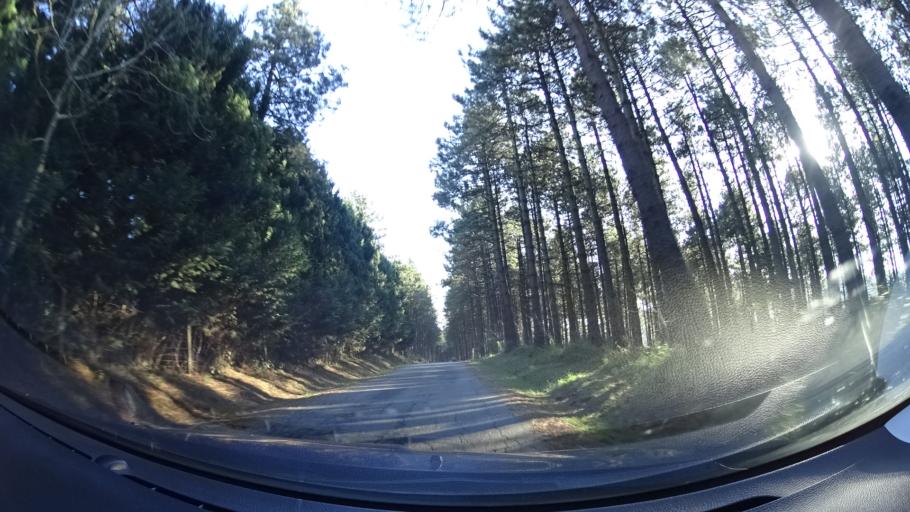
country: ES
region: Basque Country
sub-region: Bizkaia
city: Bermeo
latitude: 43.4042
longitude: -2.7597
